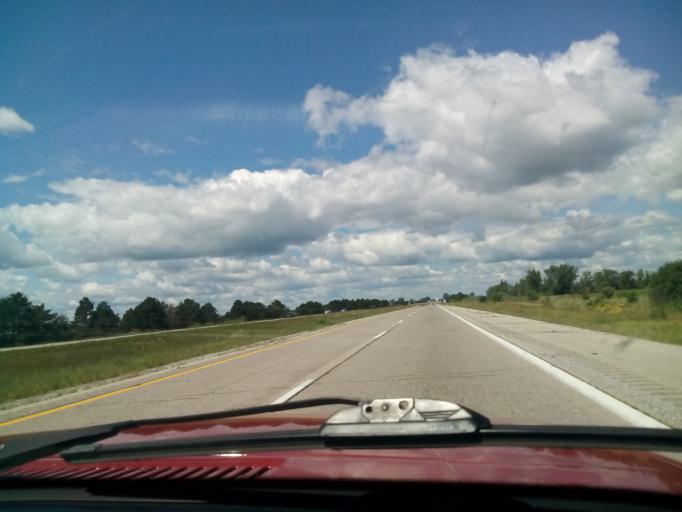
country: US
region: Michigan
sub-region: Bay County
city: Auburn
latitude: 43.6554
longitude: -83.9962
